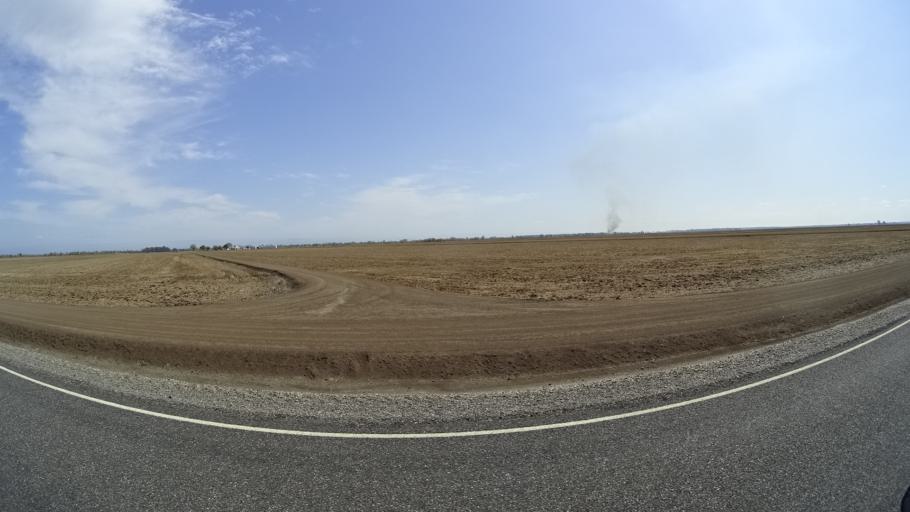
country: US
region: California
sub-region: Butte County
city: Durham
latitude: 39.5317
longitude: -121.9300
